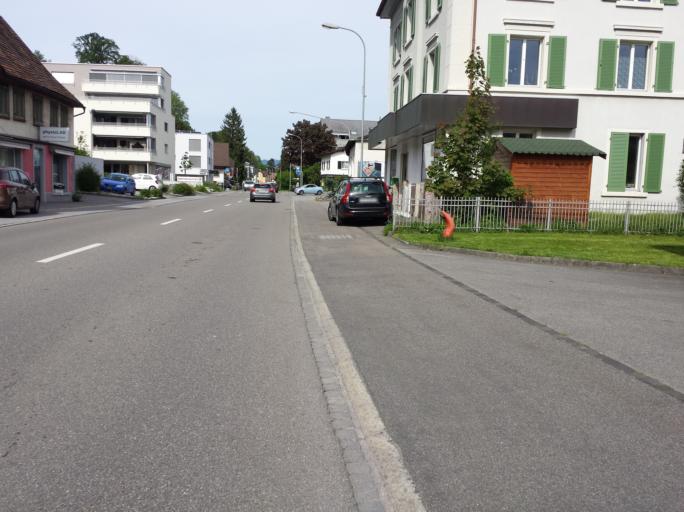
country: CH
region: Saint Gallen
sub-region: Wahlkreis Rheintal
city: Au
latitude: 47.4358
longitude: 9.6367
